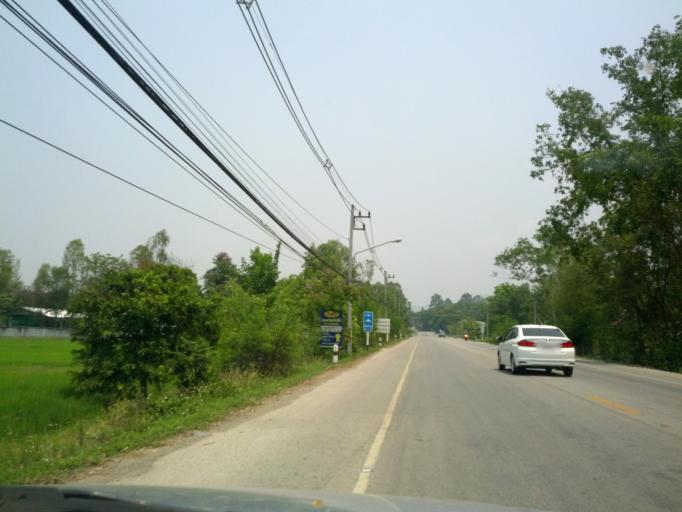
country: TH
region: Chiang Mai
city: San Sai
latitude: 18.8620
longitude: 99.1339
